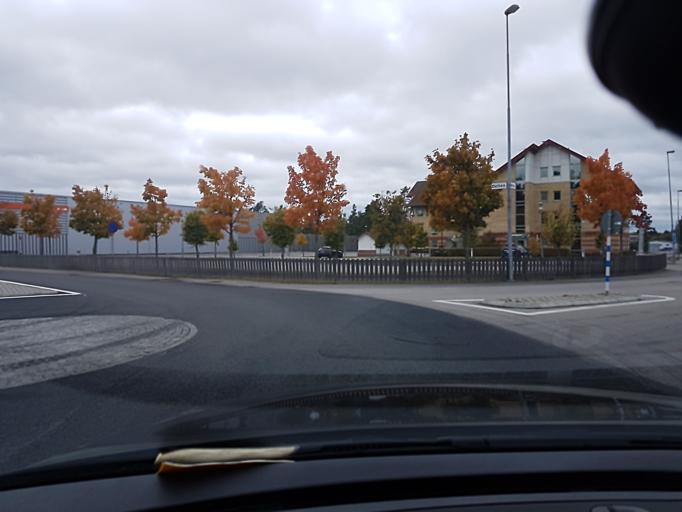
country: SE
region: Kronoberg
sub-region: Vaxjo Kommun
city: Vaexjoe
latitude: 56.9037
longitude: 14.8326
